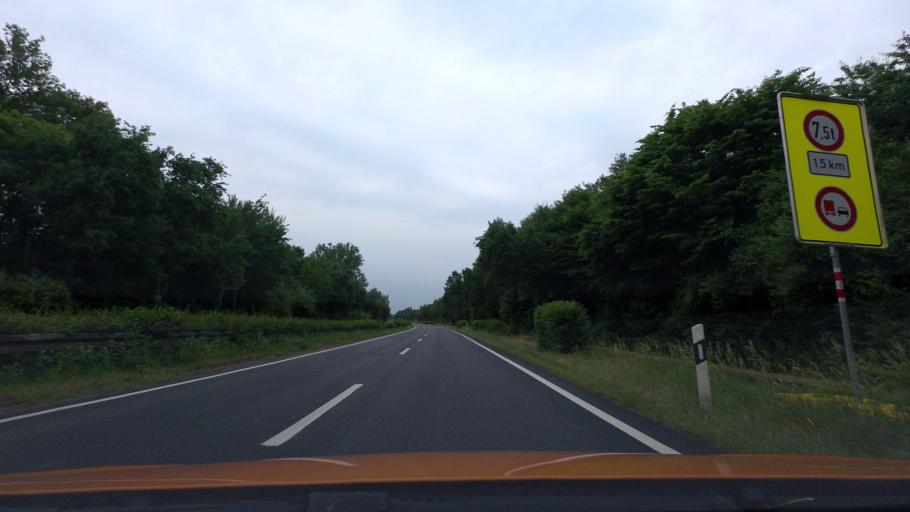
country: DE
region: Lower Saxony
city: Neustadt am Rubenberge
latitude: 52.4936
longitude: 9.4840
